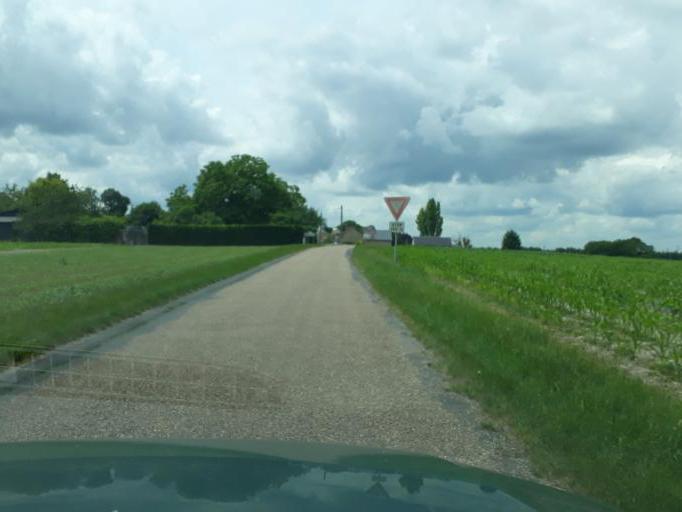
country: FR
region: Centre
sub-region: Departement du Loiret
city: Mareau-aux-Pres
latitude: 47.8720
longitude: 1.7735
